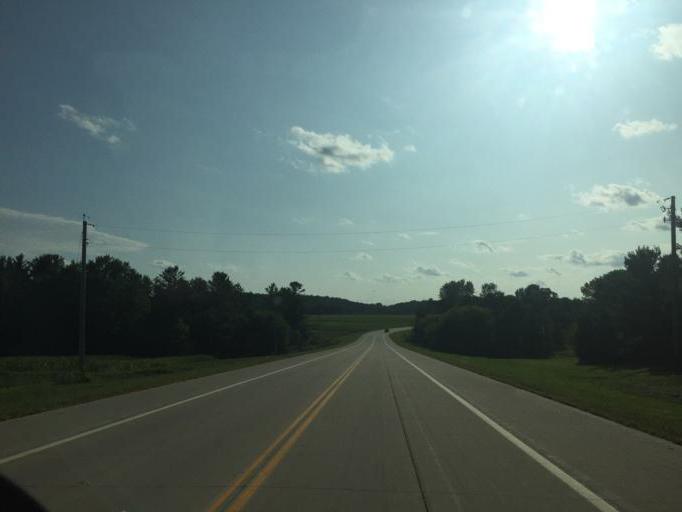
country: US
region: Minnesota
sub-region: Olmsted County
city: Rochester
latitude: 43.9978
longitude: -92.5342
